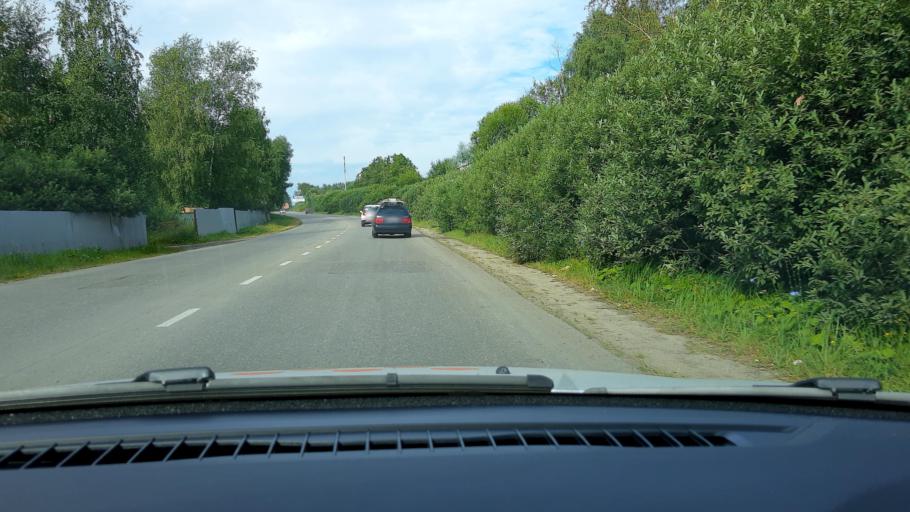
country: RU
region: Nizjnij Novgorod
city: Arzamas
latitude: 55.4204
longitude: 43.8537
